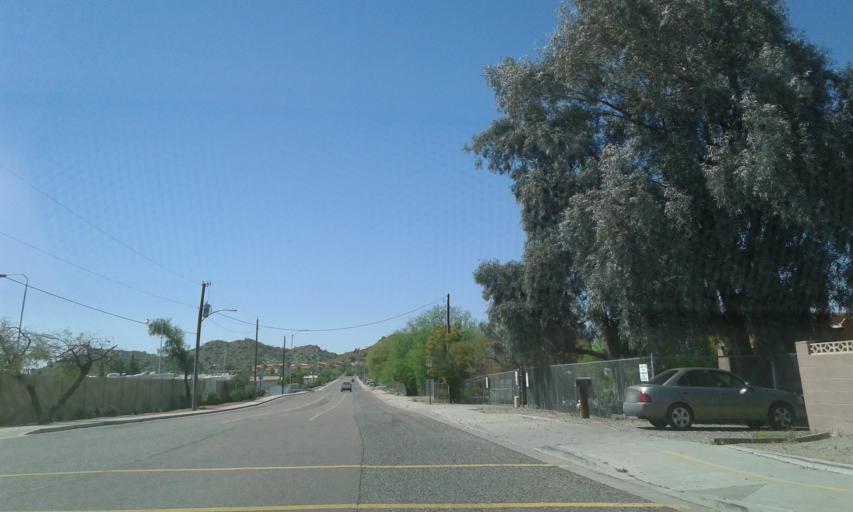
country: US
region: Arizona
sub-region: Maricopa County
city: Paradise Valley
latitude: 33.6624
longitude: -112.0220
